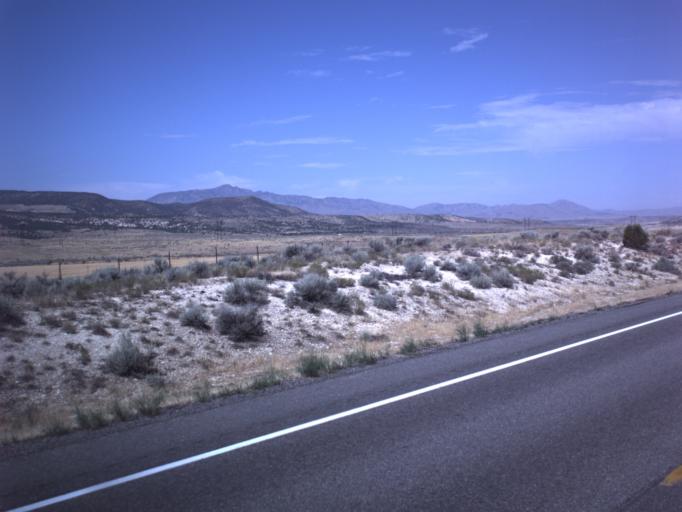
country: US
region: Utah
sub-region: Sanpete County
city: Gunnison
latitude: 39.3230
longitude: -111.9090
